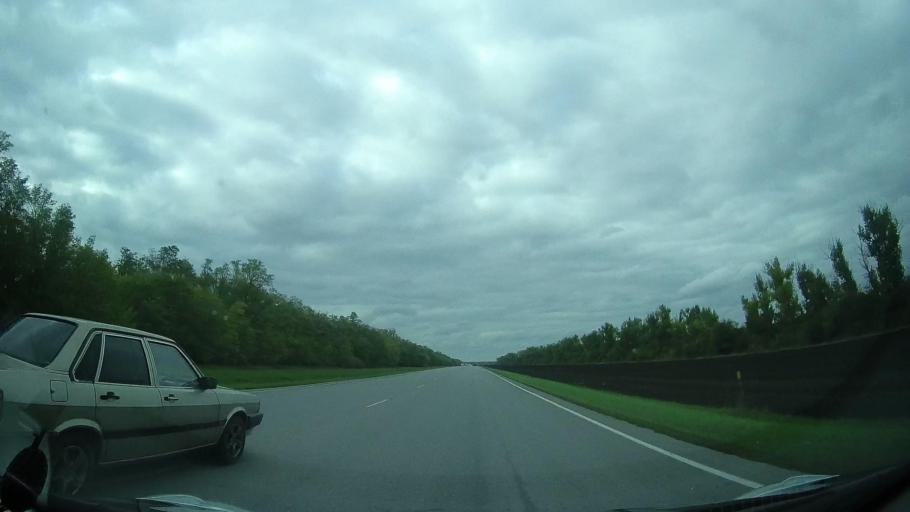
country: RU
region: Rostov
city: Yegorlykskaya
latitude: 46.6356
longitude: 40.5837
